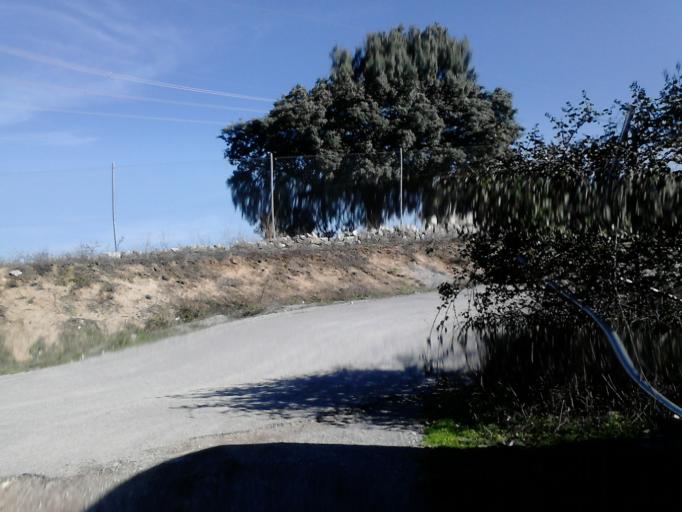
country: ES
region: Madrid
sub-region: Provincia de Madrid
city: Galapagar
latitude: 40.5756
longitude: -3.9876
